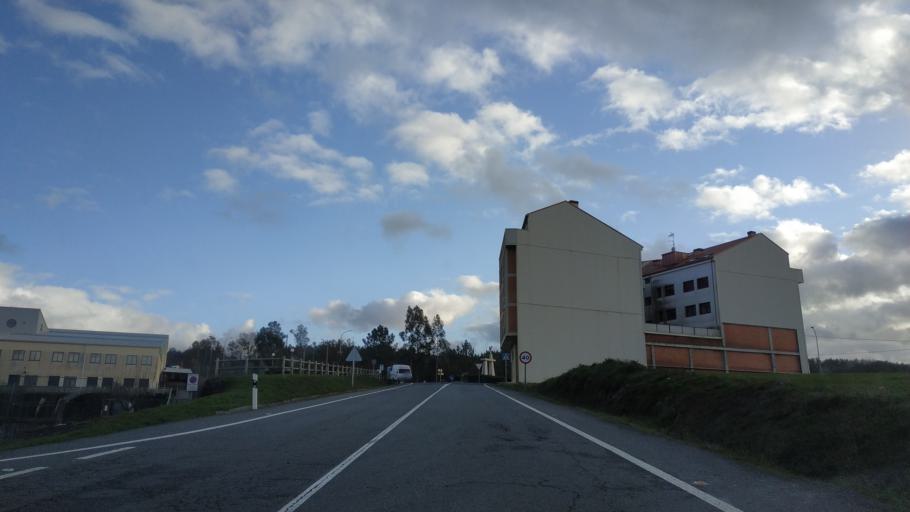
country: ES
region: Galicia
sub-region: Provincia de Pontevedra
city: Silleda
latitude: 42.7936
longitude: -8.1616
